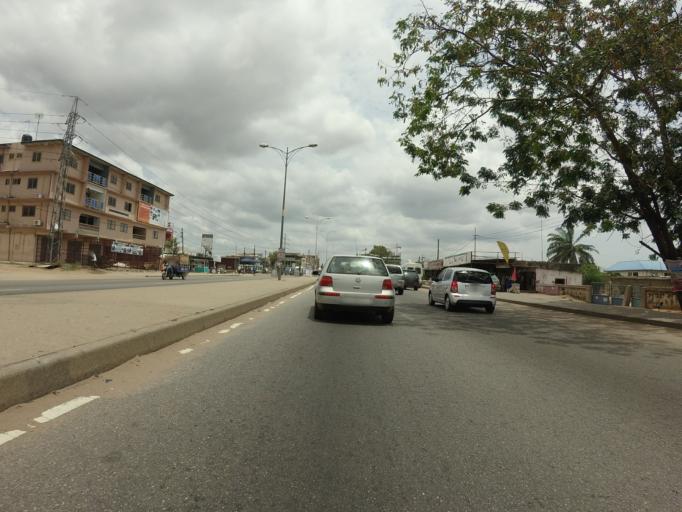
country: GH
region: Greater Accra
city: Gbawe
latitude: 5.5742
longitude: -0.2779
